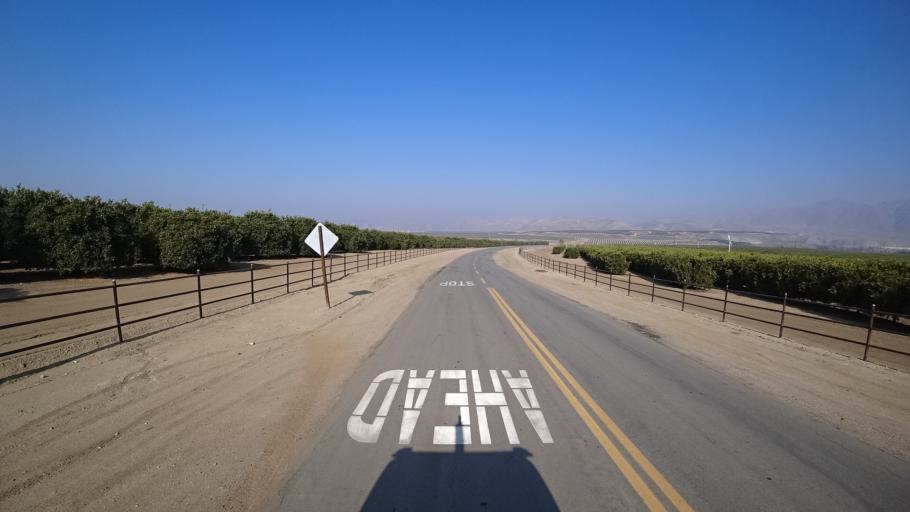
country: US
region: California
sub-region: Kern County
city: Lamont
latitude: 35.4180
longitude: -118.8322
